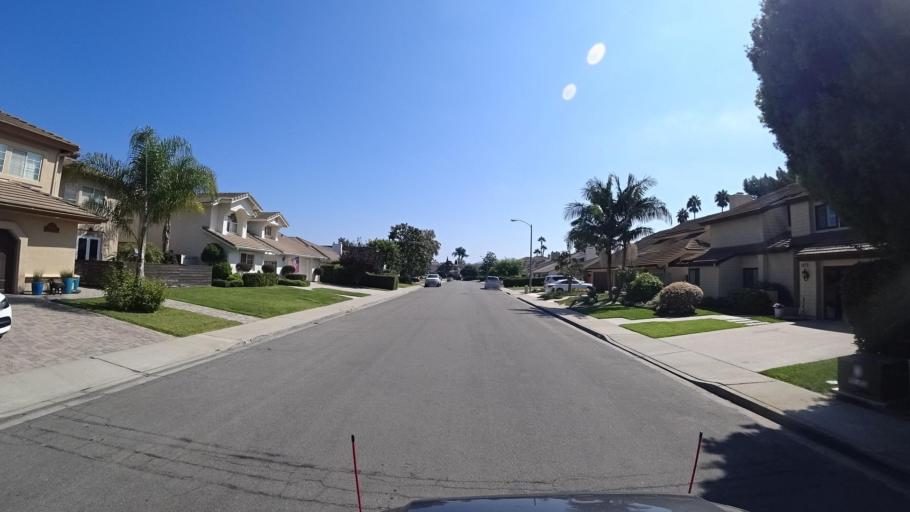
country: US
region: California
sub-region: San Diego County
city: Fairbanks Ranch
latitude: 32.9873
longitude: -117.2133
